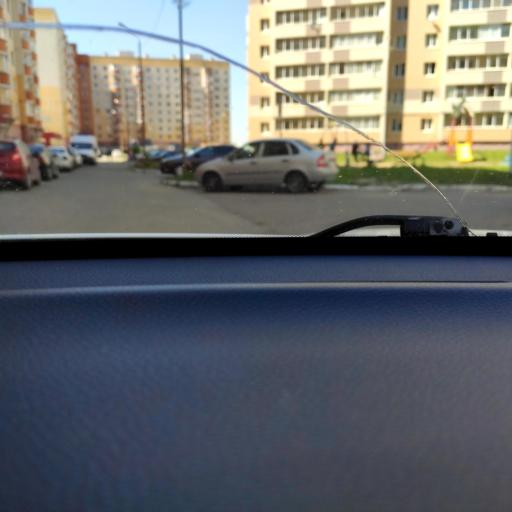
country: RU
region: Tatarstan
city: Osinovo
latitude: 55.8701
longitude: 48.8783
